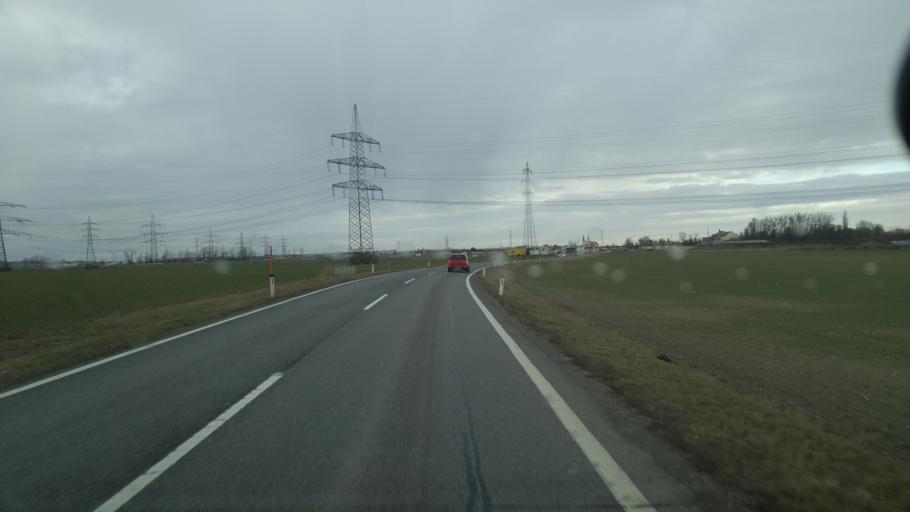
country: AT
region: Lower Austria
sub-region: Politischer Bezirk Modling
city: Achau
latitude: 48.0879
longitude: 16.4071
